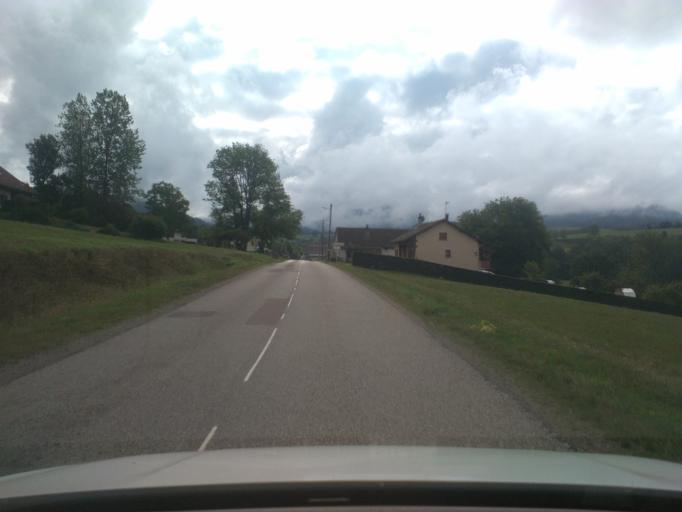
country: FR
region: Lorraine
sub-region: Departement des Vosges
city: Senones
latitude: 48.3470
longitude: 6.9522
